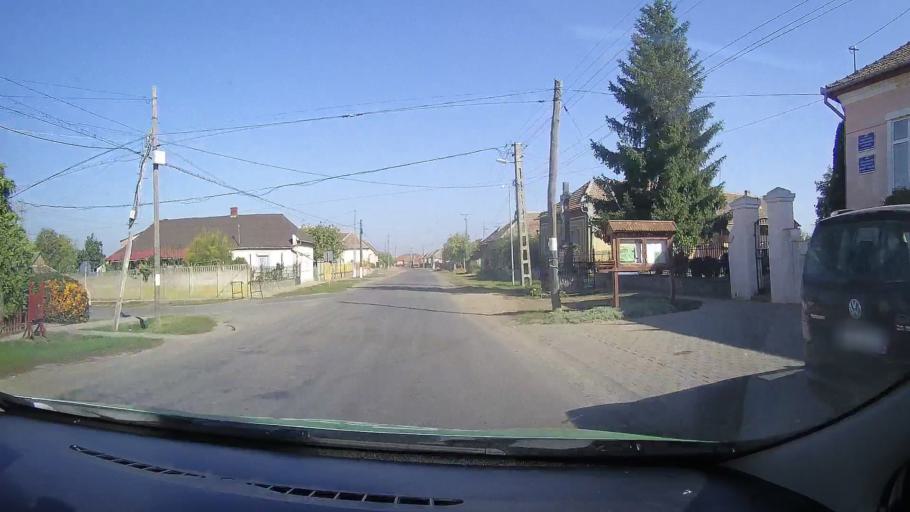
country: RO
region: Satu Mare
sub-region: Comuna Ciumesti
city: Ciumesti
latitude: 47.6612
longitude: 22.3354
